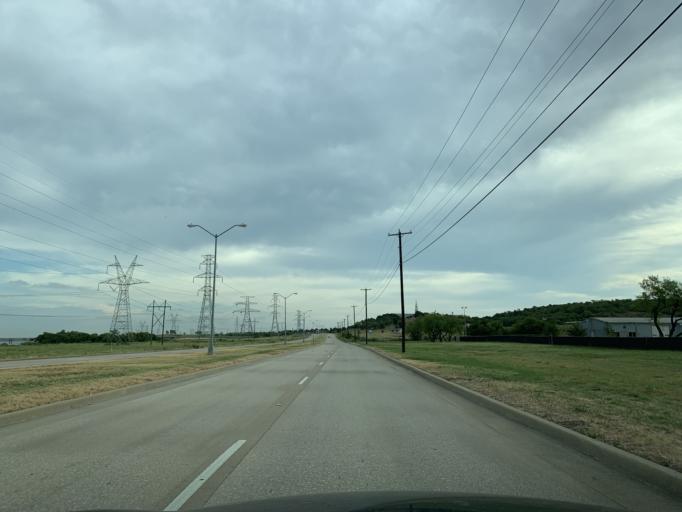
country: US
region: Texas
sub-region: Dallas County
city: Grand Prairie
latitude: 32.7013
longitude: -96.9582
